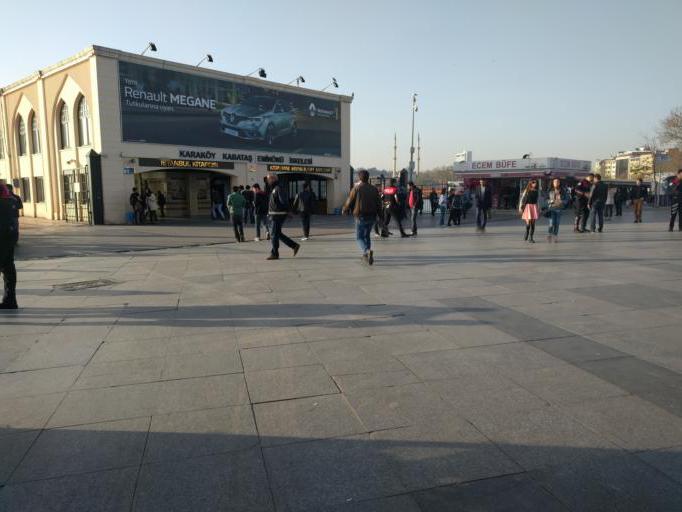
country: TR
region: Istanbul
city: UEskuedar
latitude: 40.9924
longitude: 29.0235
